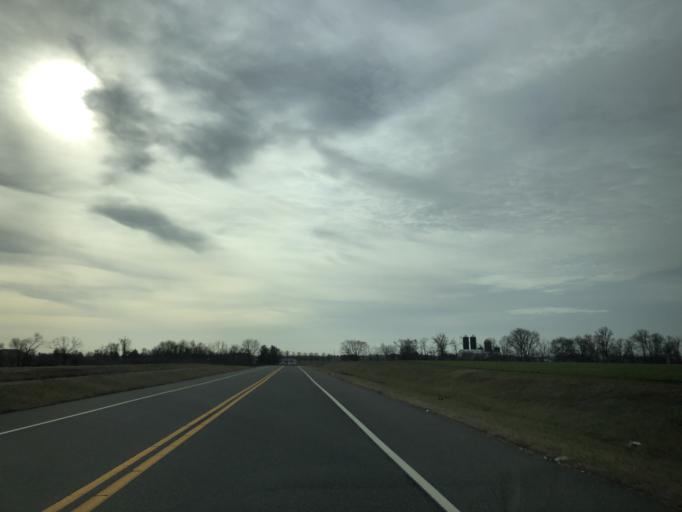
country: US
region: Delaware
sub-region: New Castle County
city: Middletown
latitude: 39.5175
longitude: -75.6789
